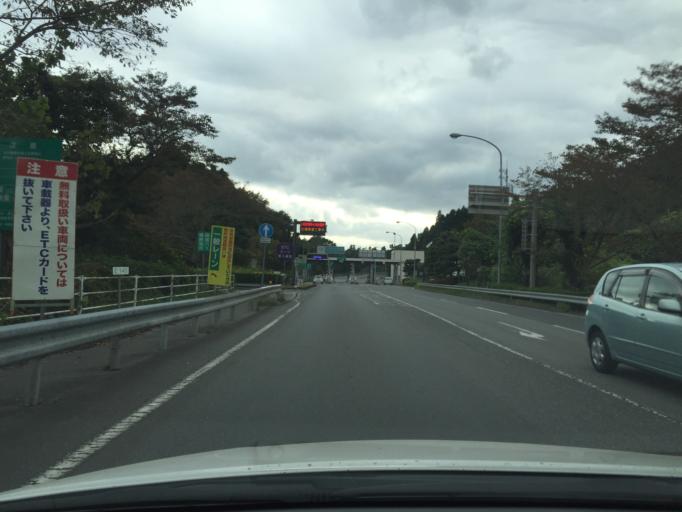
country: JP
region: Ibaraki
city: Kitaibaraki
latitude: 36.9044
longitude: 140.7531
